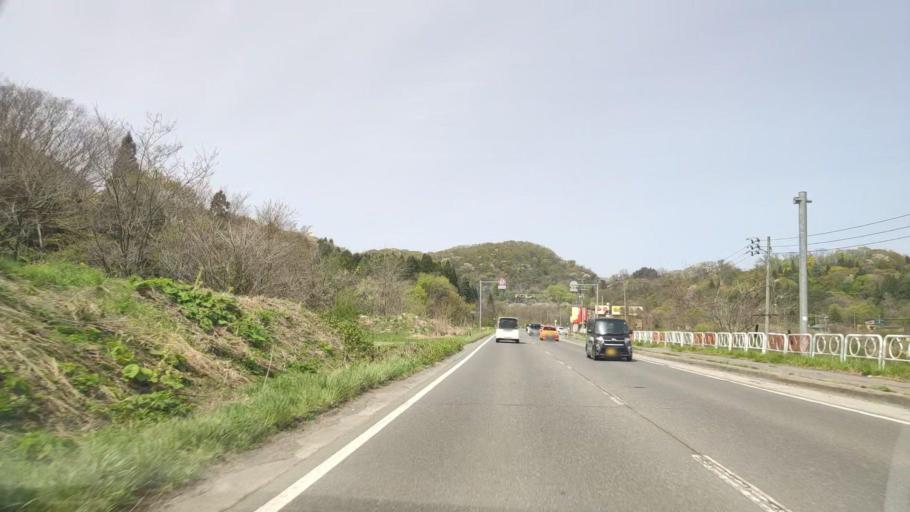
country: JP
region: Aomori
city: Aomori Shi
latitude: 40.8511
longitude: 140.8382
